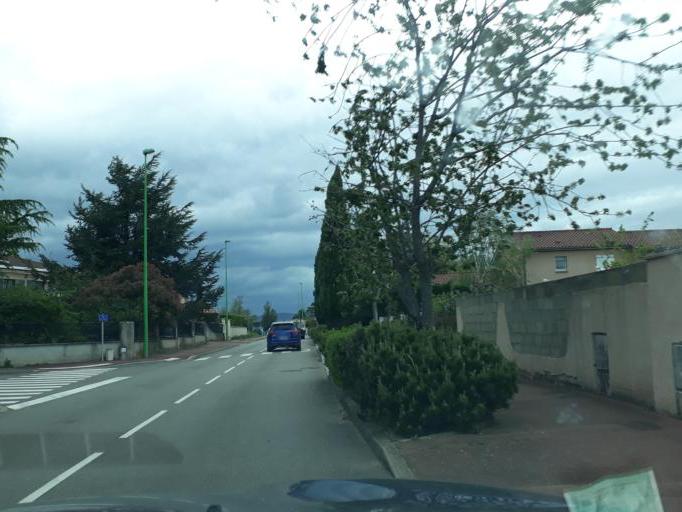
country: FR
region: Rhone-Alpes
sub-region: Departement du Rhone
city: Soucieu-en-Jarrest
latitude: 45.6760
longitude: 4.6946
